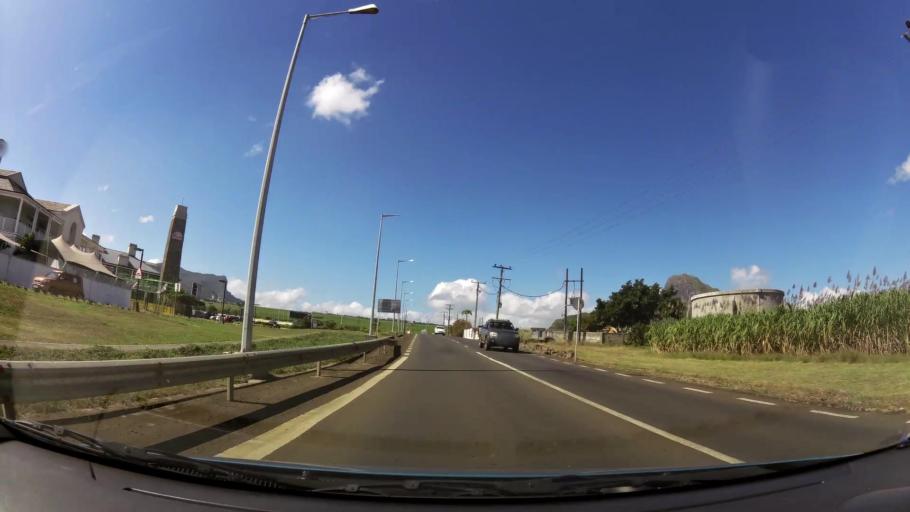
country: MU
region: Black River
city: Cascavelle
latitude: -20.2801
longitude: 57.4021
